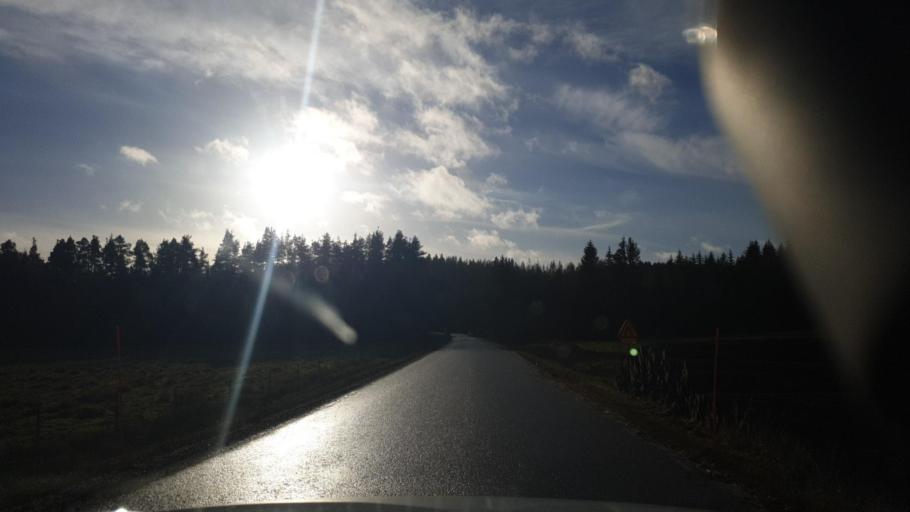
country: SE
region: Vaermland
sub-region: Eda Kommun
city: Charlottenberg
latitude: 59.8140
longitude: 12.1628
